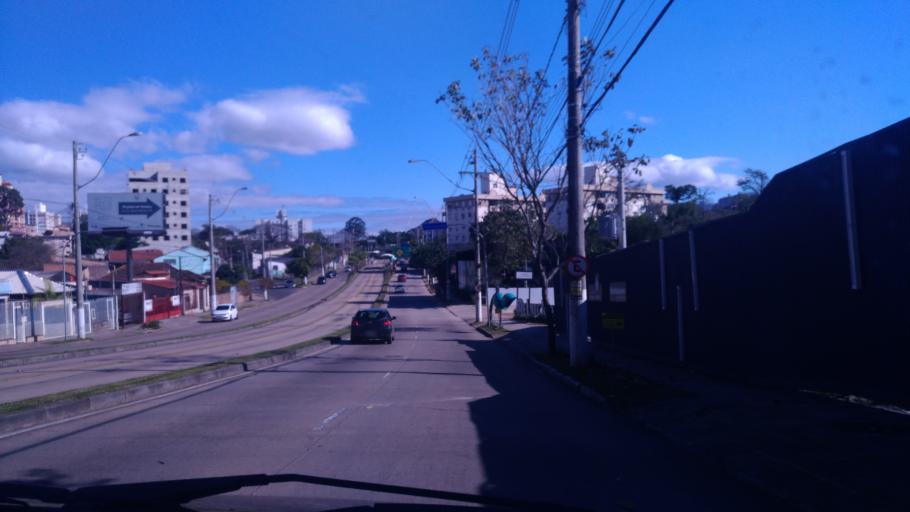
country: BR
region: Rio Grande do Sul
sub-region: Porto Alegre
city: Porto Alegre
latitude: -30.0751
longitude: -51.2048
